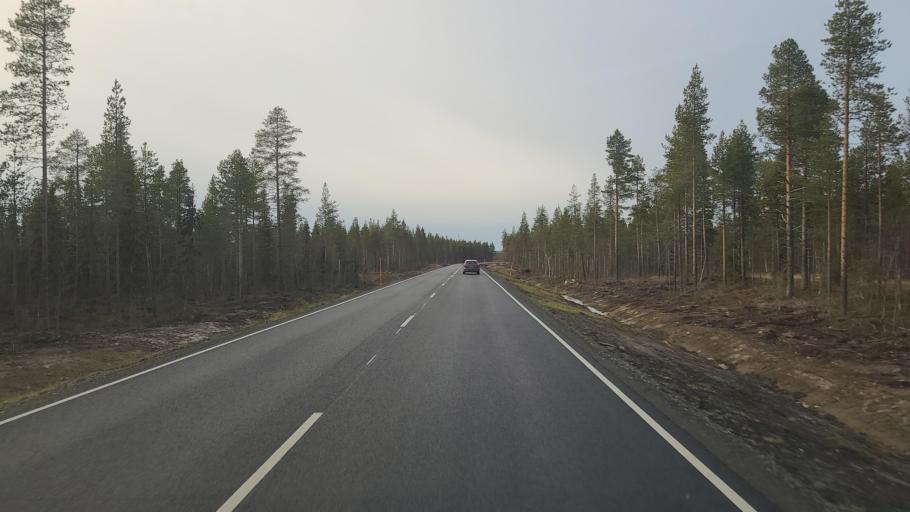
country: FI
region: Lapland
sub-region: Tunturi-Lappi
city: Kittilae
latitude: 67.8707
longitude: 24.9097
